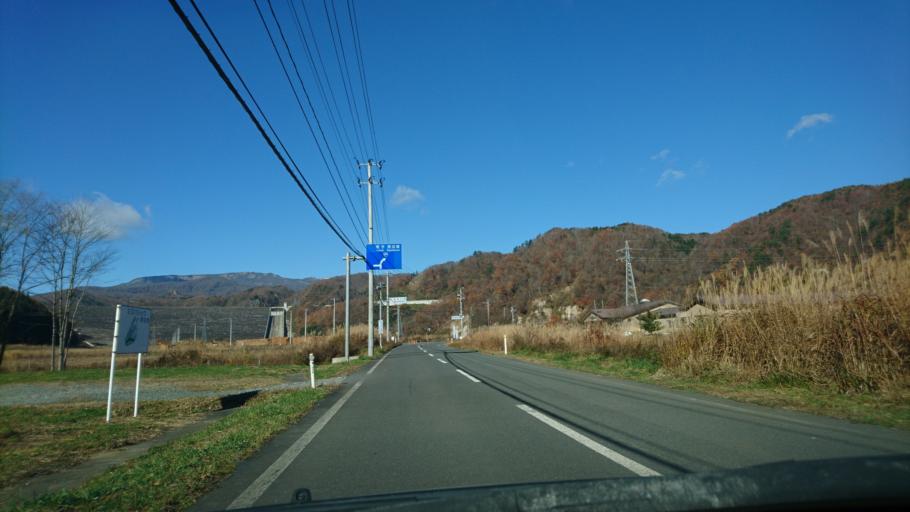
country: JP
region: Iwate
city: Mizusawa
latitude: 39.1188
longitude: 140.9357
